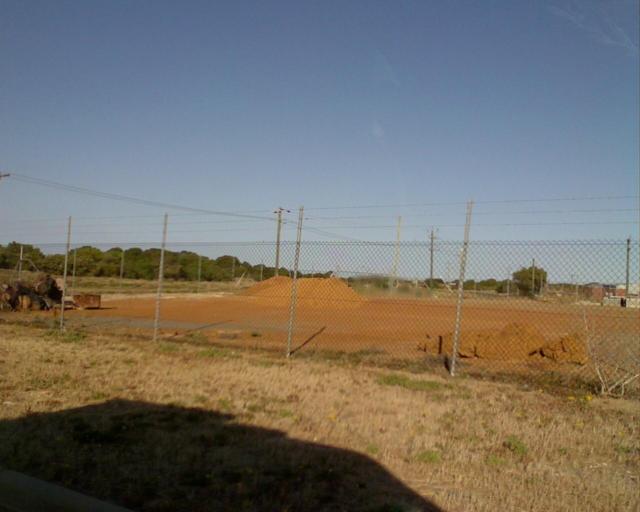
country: AU
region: Western Australia
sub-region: Dandaragan
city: Jurien Bay
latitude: -30.0537
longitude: 114.9784
